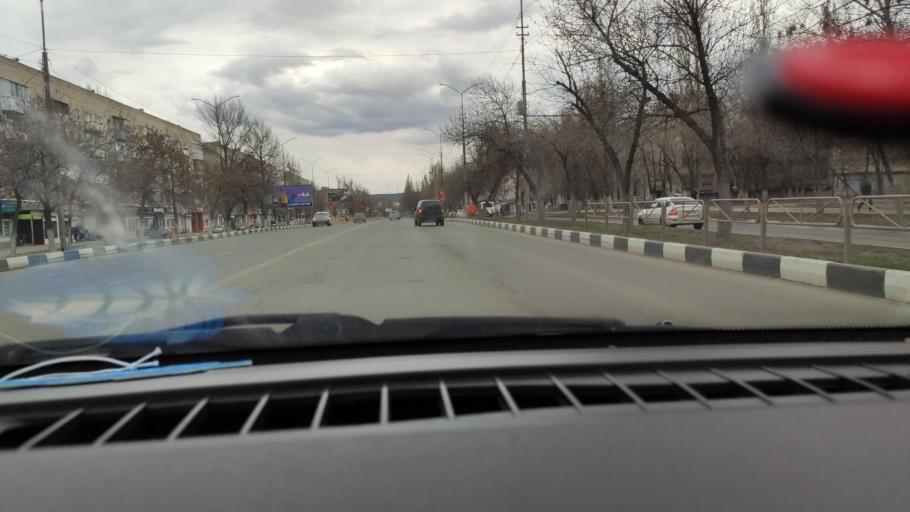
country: RU
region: Saratov
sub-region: Saratovskiy Rayon
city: Saratov
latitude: 51.5991
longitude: 45.9685
